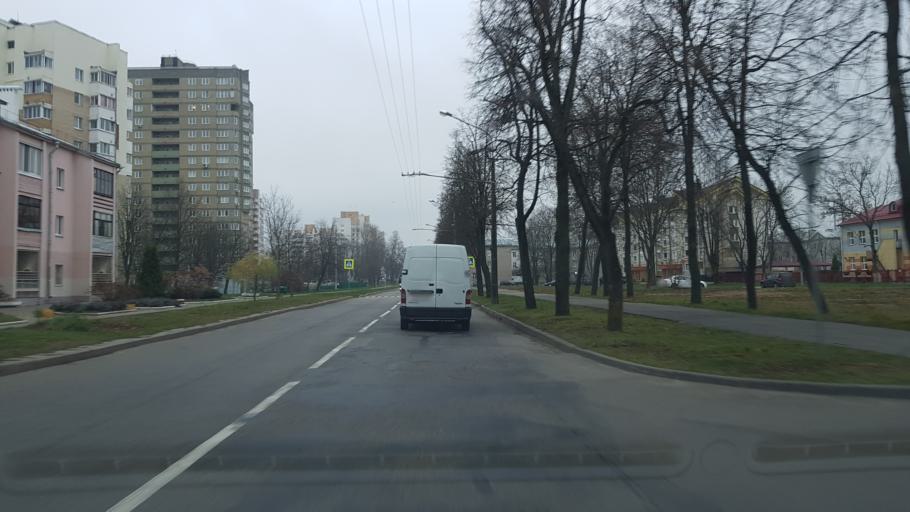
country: BY
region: Minsk
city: Minsk
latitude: 53.9289
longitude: 27.5418
